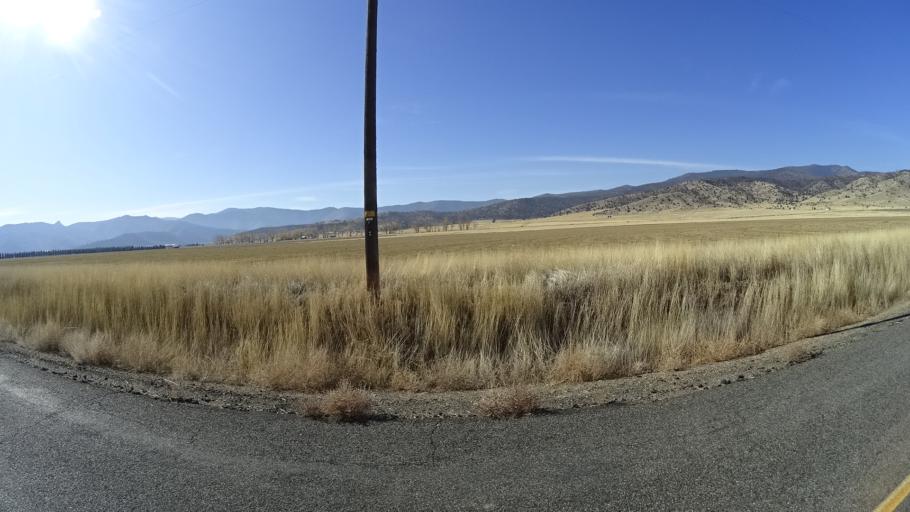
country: US
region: California
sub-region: Siskiyou County
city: Montague
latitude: 41.5617
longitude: -122.5475
